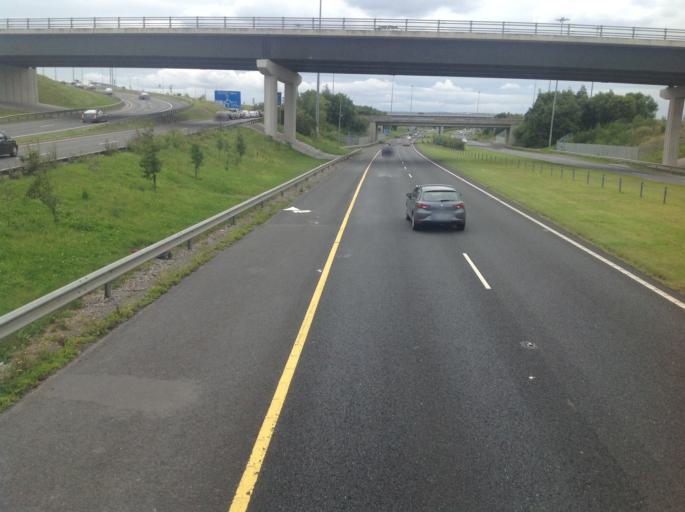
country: IE
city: Bonnybrook
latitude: 53.4128
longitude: -6.2250
